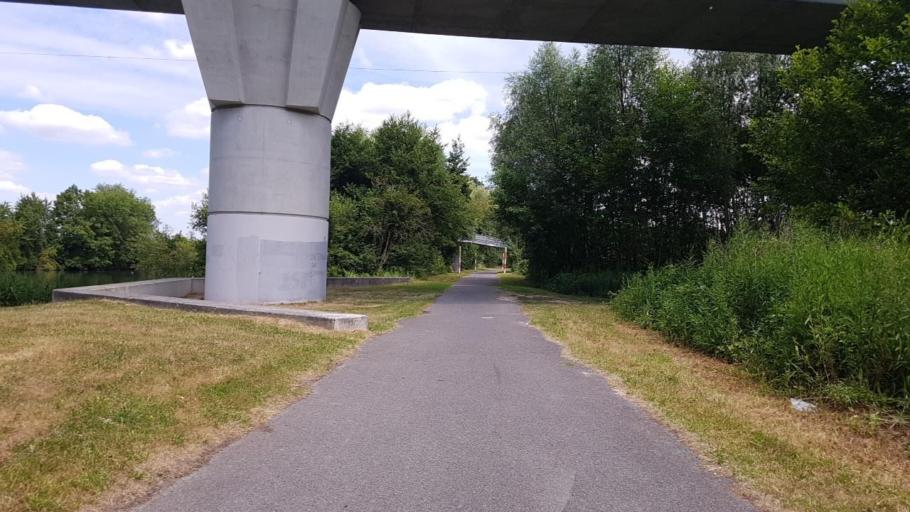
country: FR
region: Picardie
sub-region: Departement de l'Oise
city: Choisy-au-Bac
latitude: 49.4336
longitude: 2.8655
